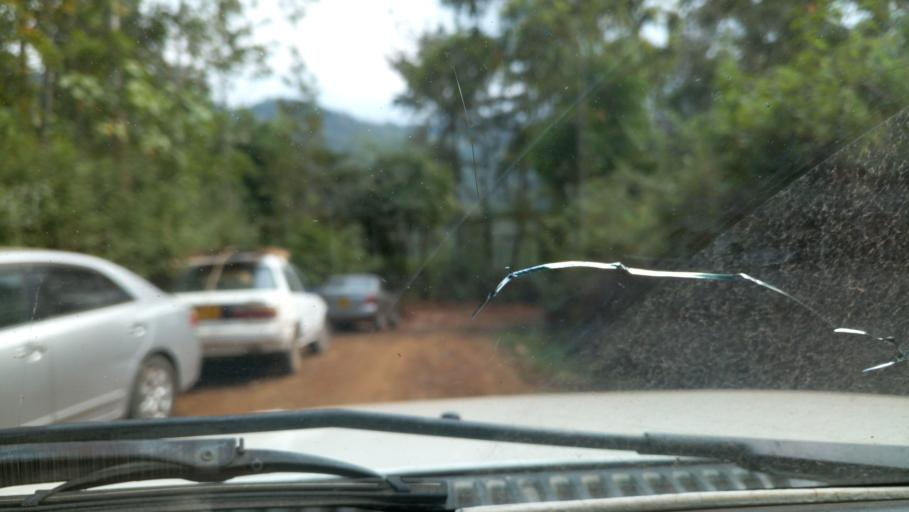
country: KE
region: Murang'a District
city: Kangema
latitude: -0.6375
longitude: 37.0146
